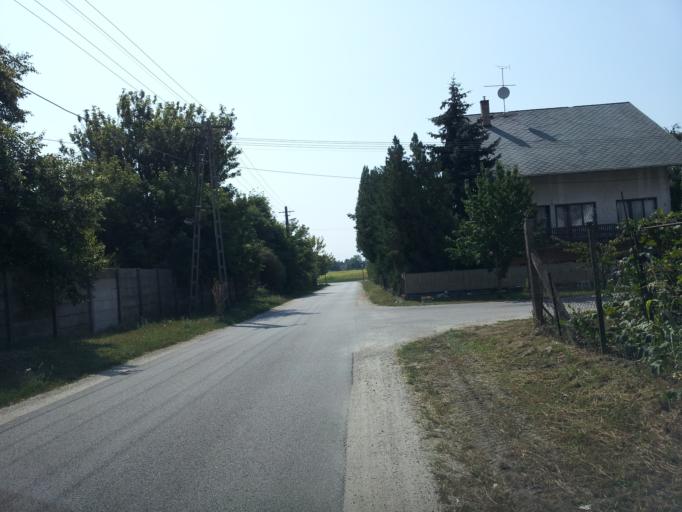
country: HU
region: Pest
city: Dunavarsany
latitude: 47.2870
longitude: 19.0366
